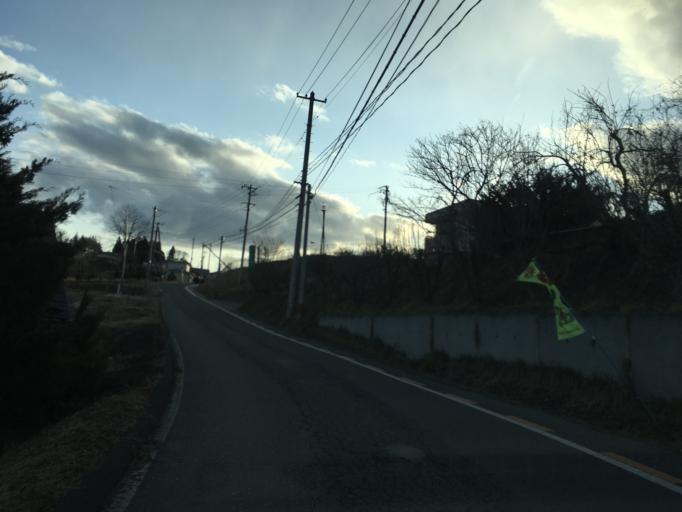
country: JP
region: Iwate
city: Ichinoseki
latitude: 38.8666
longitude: 141.3535
